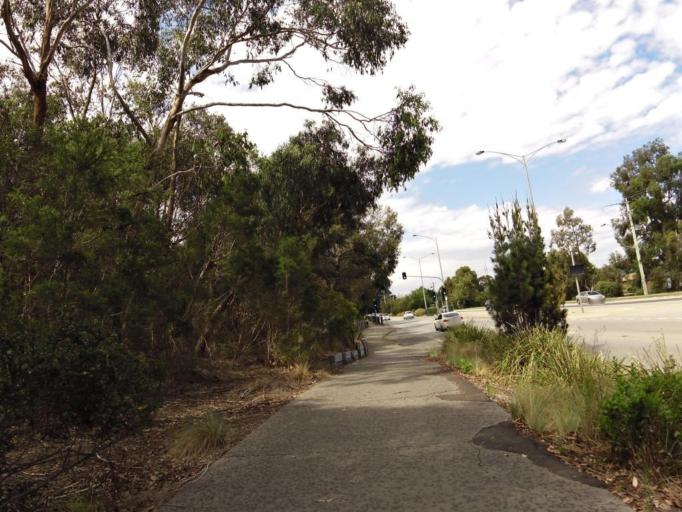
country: AU
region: Victoria
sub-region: Knox
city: Rowville
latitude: -37.9275
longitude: 145.2404
